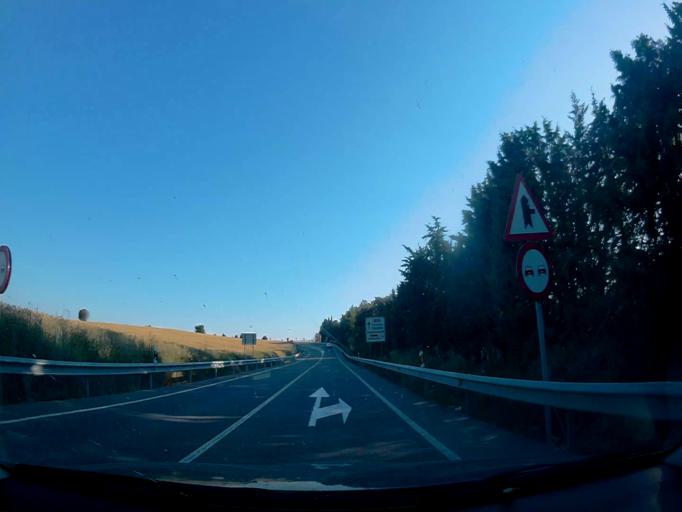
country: ES
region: Castille-La Mancha
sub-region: Province of Toledo
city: Escalona
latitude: 40.1240
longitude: -4.4080
